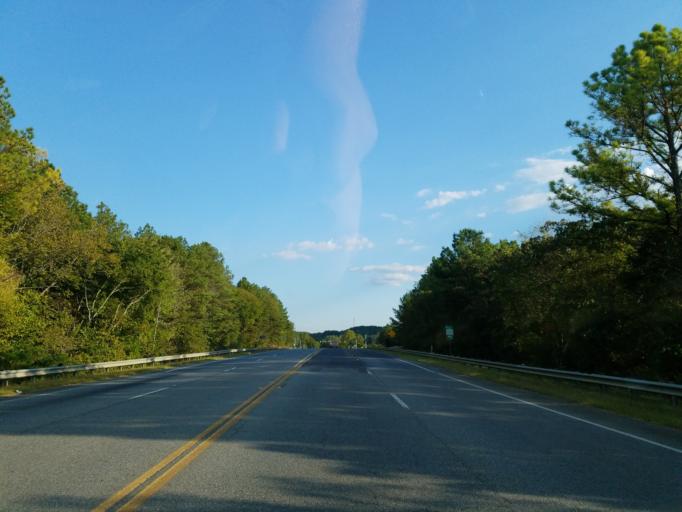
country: US
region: Georgia
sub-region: Murray County
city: Chatsworth
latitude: 34.6996
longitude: -84.7399
